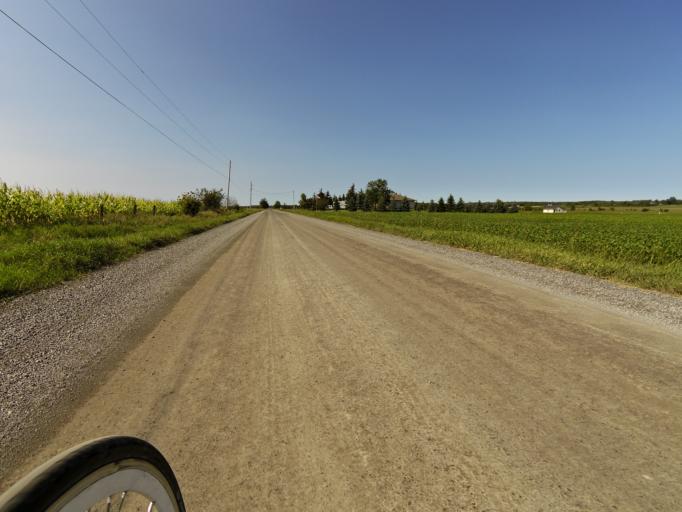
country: CA
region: Ontario
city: Arnprior
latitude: 45.3683
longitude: -76.1353
